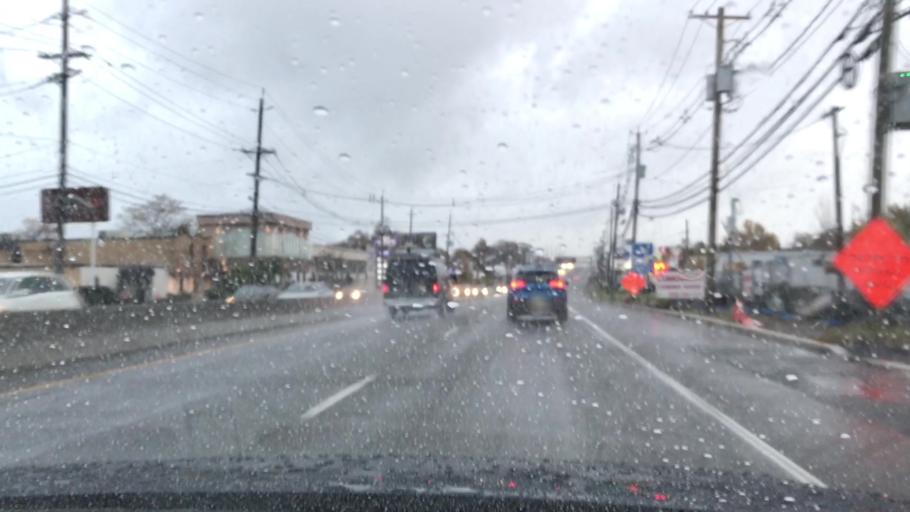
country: US
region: New Jersey
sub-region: Bergen County
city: Lodi
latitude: 40.8801
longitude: -74.0792
